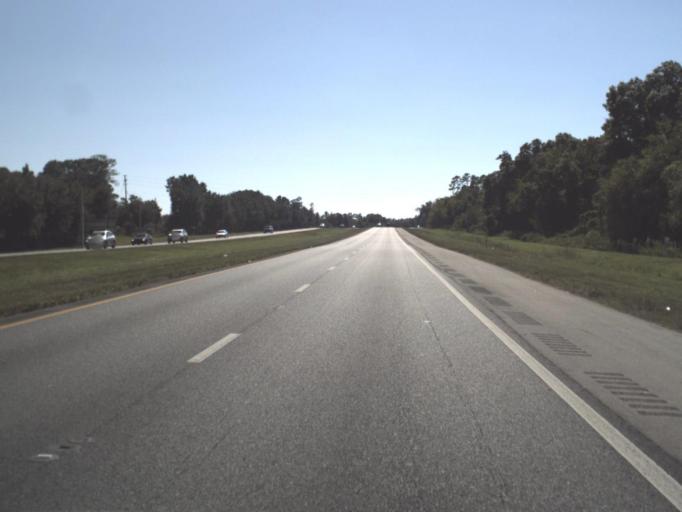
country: US
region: Florida
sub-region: Seminole County
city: Oviedo
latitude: 28.6358
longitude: -81.2435
